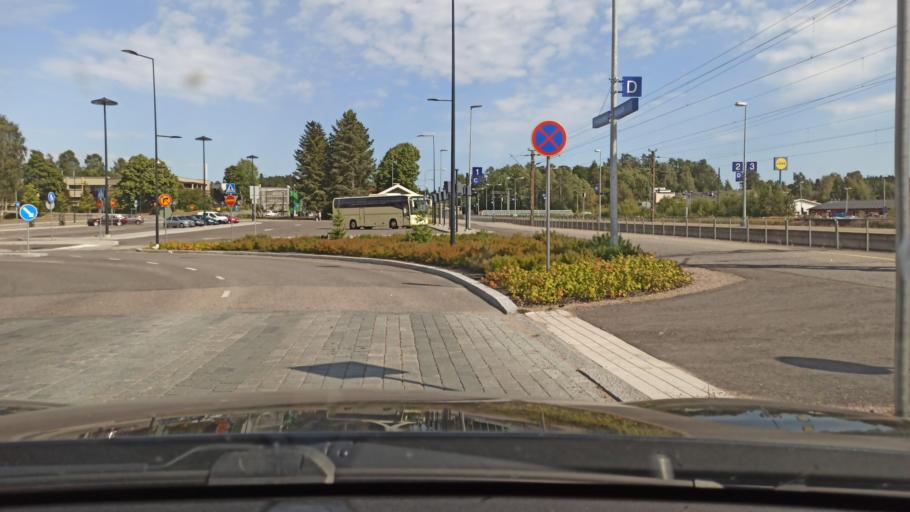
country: FI
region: Uusimaa
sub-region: Helsinki
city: Kirkkonummi
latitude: 60.1199
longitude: 24.4348
